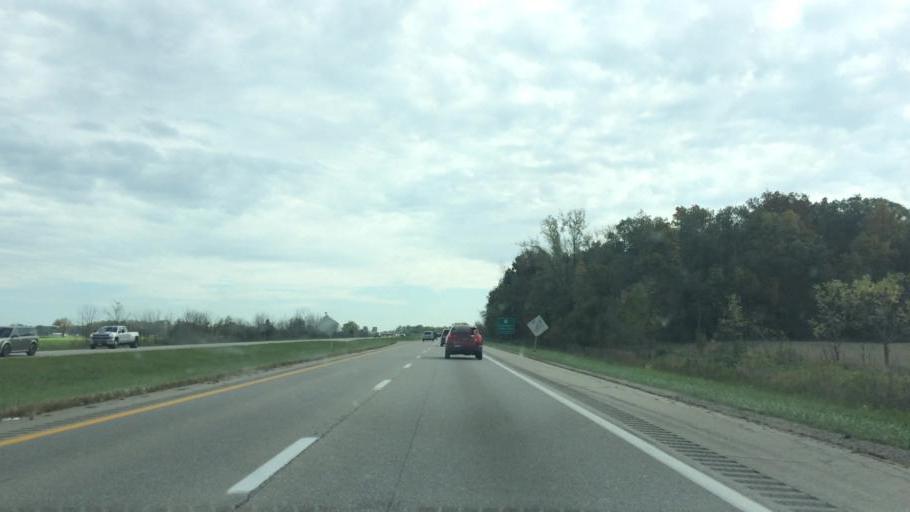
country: US
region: Ohio
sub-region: Union County
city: New California
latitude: 40.1704
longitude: -83.2410
